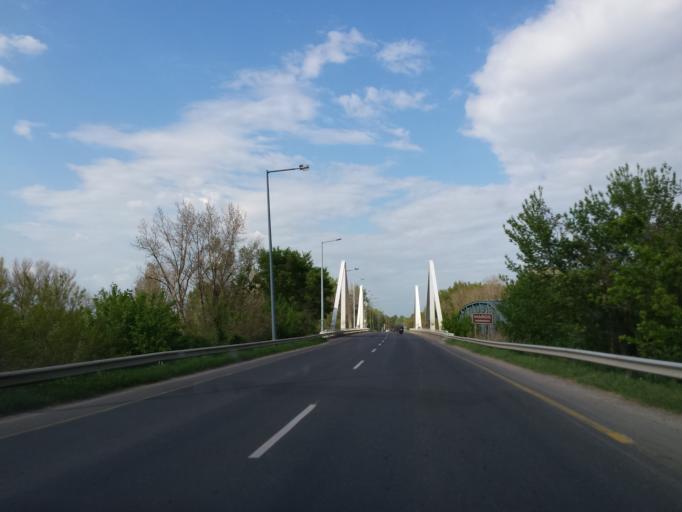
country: HU
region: Csongrad
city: Kiszombor
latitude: 46.2017
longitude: 20.4528
